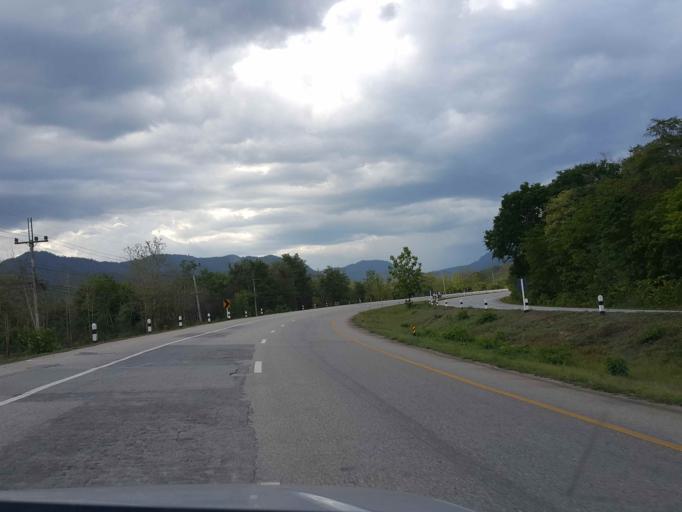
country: TH
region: Lampang
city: Thoen
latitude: 17.7425
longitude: 99.2311
